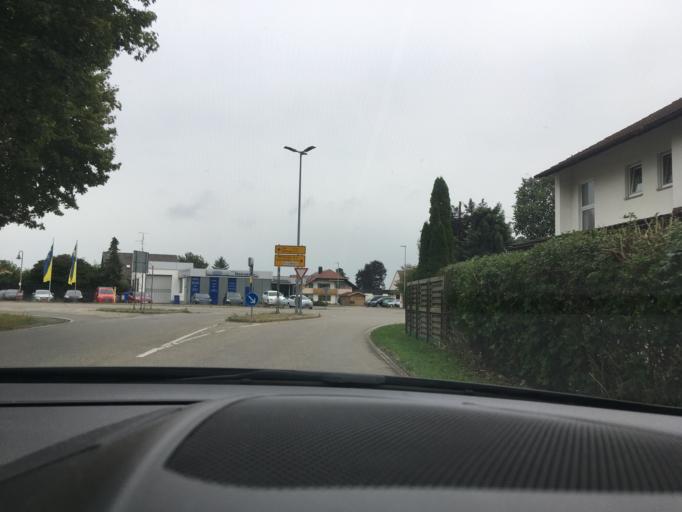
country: DE
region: Baden-Wuerttemberg
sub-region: Tuebingen Region
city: Kirchdorf
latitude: 48.0805
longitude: 10.1213
